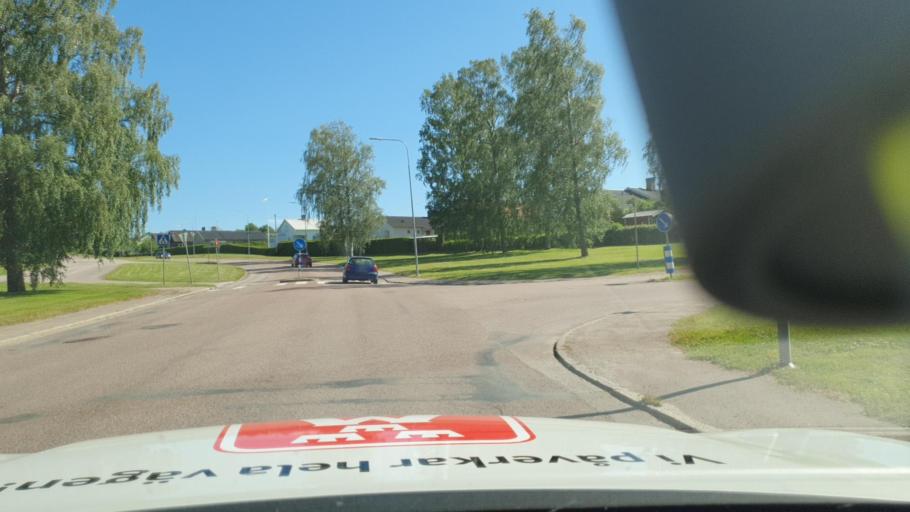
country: SE
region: Vaermland
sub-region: Kristinehamns Kommun
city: Kristinehamn
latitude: 59.3024
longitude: 14.0898
